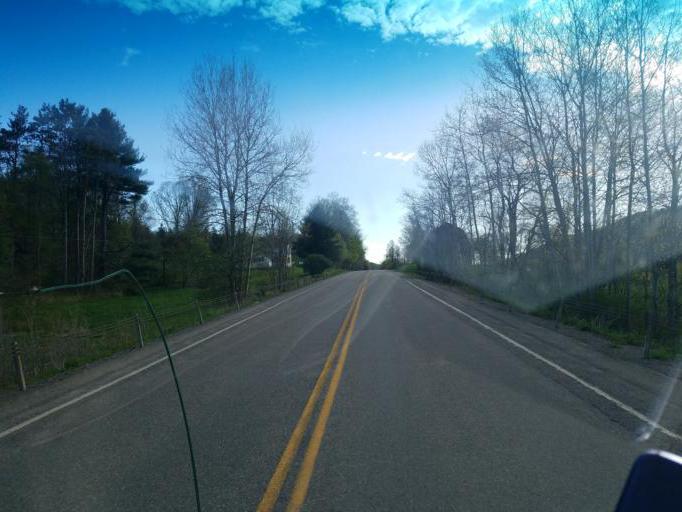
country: US
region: New York
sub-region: Allegany County
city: Wellsville
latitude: 42.0059
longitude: -77.8488
